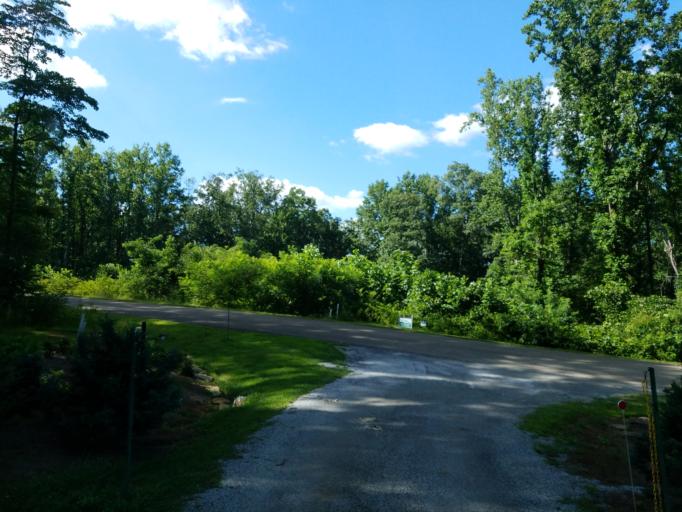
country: US
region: Georgia
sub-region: Pickens County
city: Jasper
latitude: 34.5327
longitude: -84.3956
